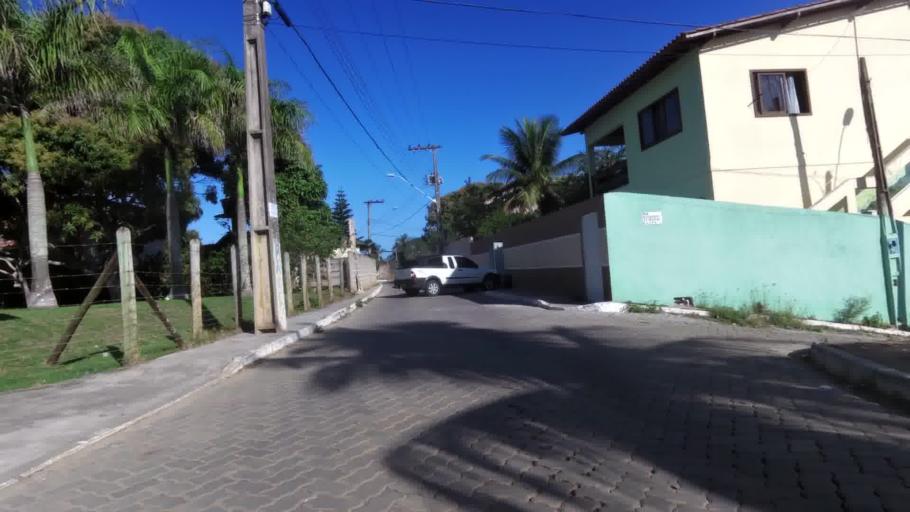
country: BR
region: Espirito Santo
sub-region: Guarapari
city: Guarapari
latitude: -20.7494
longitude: -40.5617
